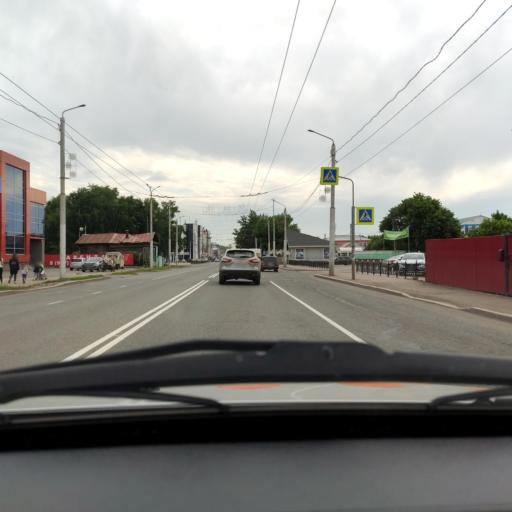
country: RU
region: Bashkortostan
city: Sterlitamak
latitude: 53.6160
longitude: 55.9577
